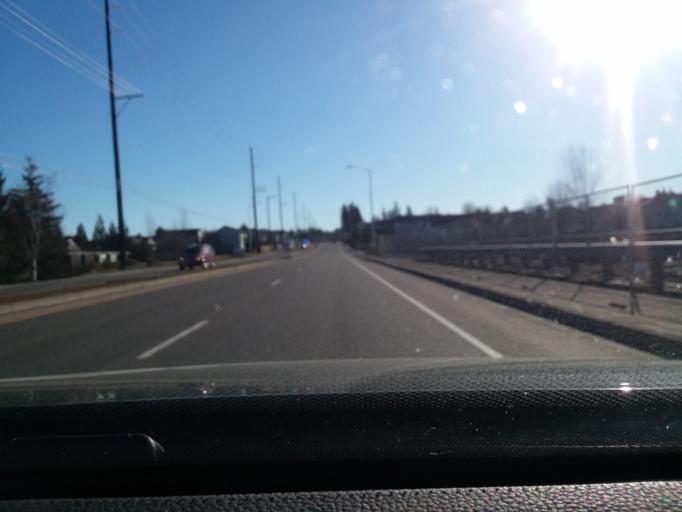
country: US
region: Washington
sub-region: Pierce County
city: Frederickson
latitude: 47.0965
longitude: -122.3140
